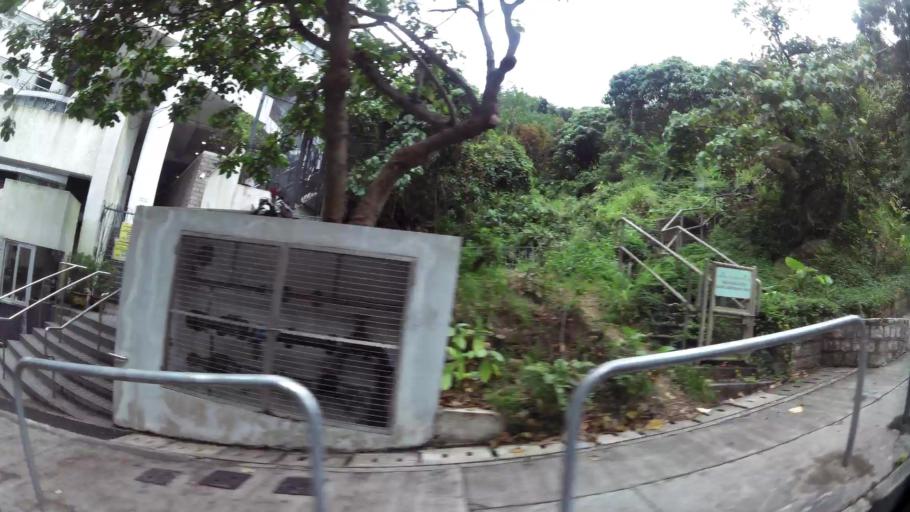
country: HK
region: Central and Western
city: Central
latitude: 22.2513
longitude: 114.1564
